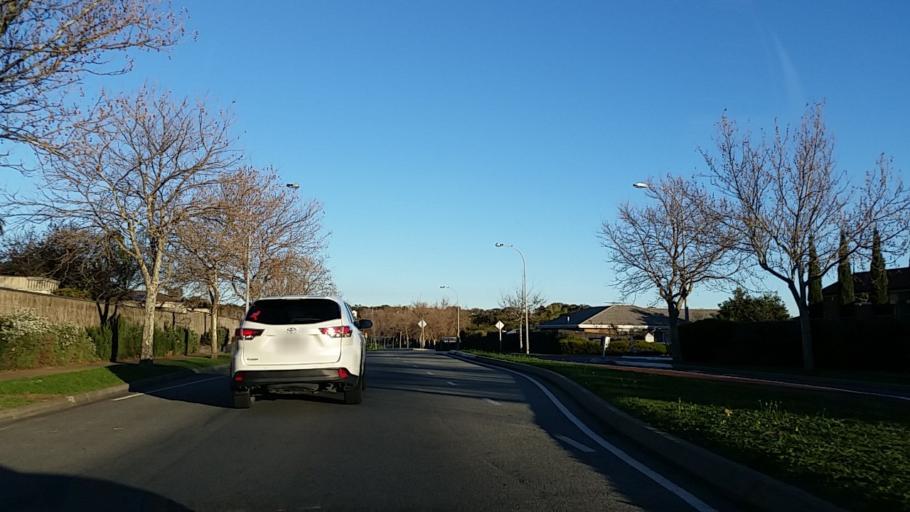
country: AU
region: South Australia
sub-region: Onkaparinga
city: Moana
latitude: -35.1968
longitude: 138.4848
